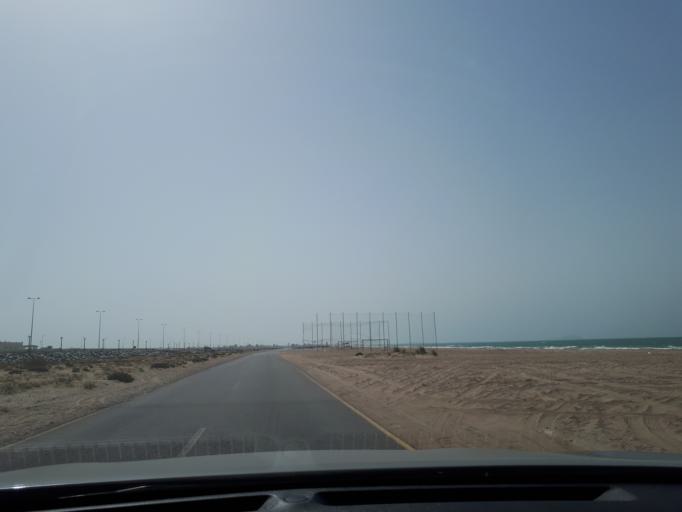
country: OM
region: Al Batinah
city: Barka'
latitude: 23.7141
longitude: 57.8718
